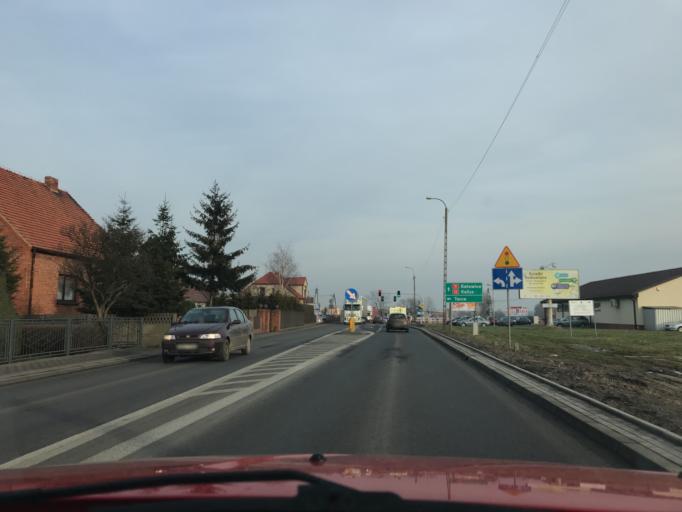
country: PL
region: Greater Poland Voivodeship
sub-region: Powiat jarocinski
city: Witaszyce
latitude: 51.9426
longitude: 17.5690
